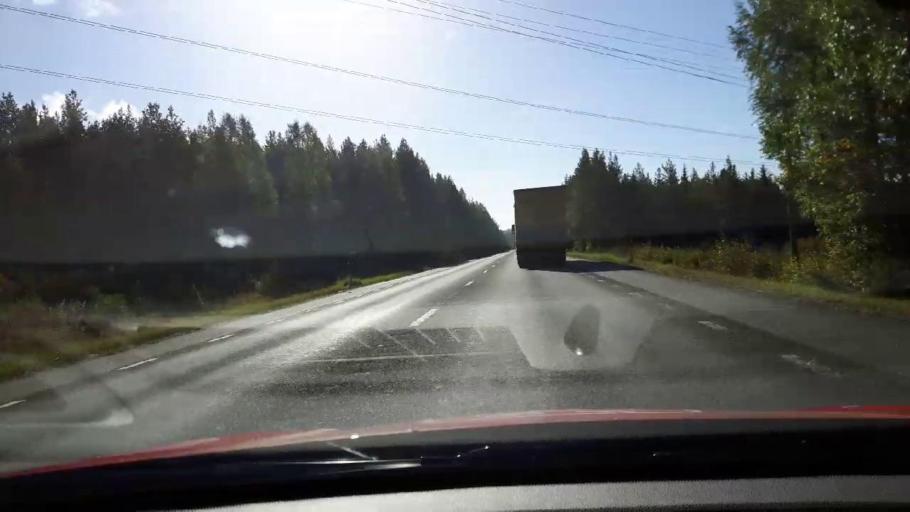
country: SE
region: Jaemtland
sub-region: Braecke Kommun
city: Braecke
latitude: 62.7241
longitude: 15.4451
